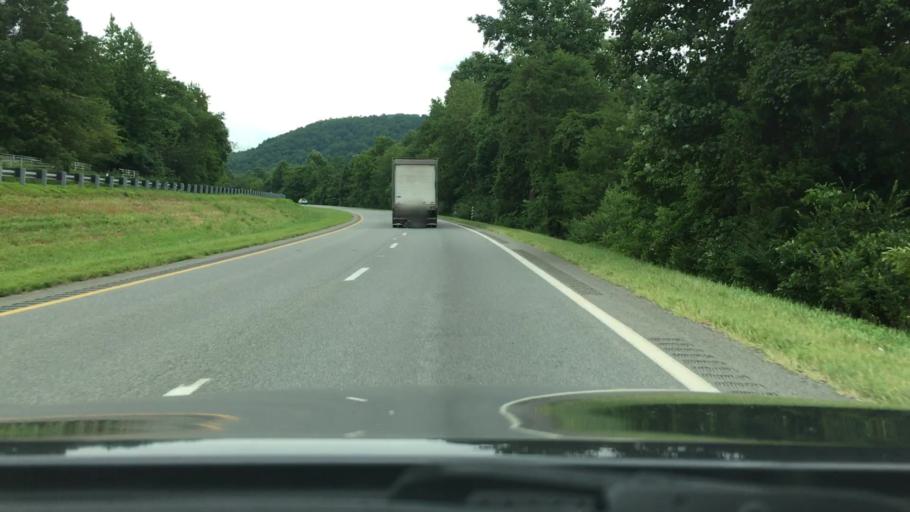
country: US
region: Virginia
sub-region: Albemarle County
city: Crozet
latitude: 37.9781
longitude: -78.6020
